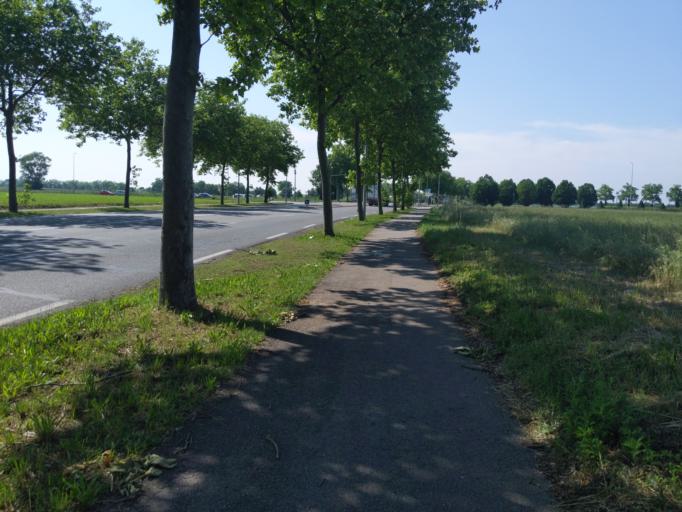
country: FR
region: Rhone-Alpes
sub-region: Departement du Rhone
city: Bron
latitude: 45.7460
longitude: 4.9369
